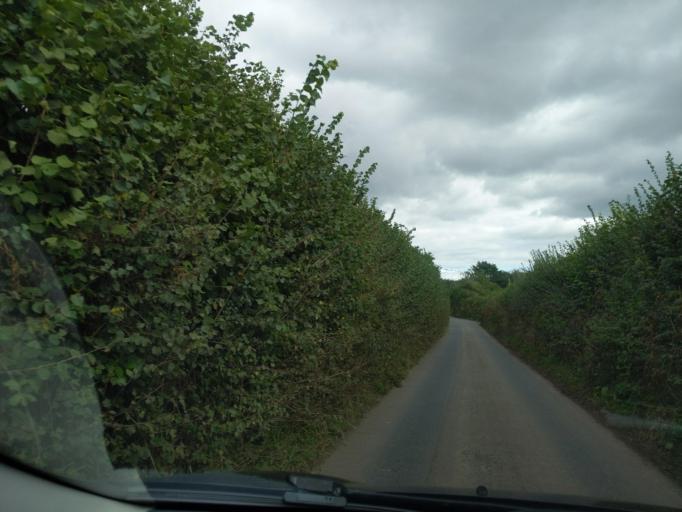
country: GB
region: England
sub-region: Plymouth
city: Plymstock
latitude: 50.3442
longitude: -4.0812
